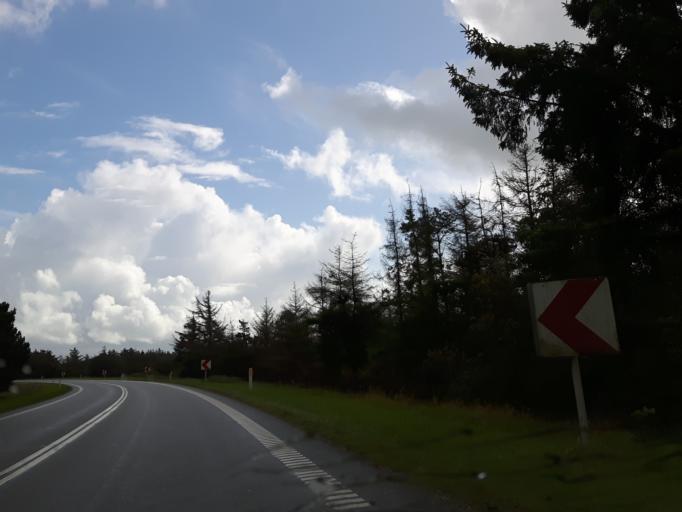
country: DK
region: Central Jutland
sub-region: Struer Kommune
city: Struer
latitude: 56.5862
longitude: 8.5285
